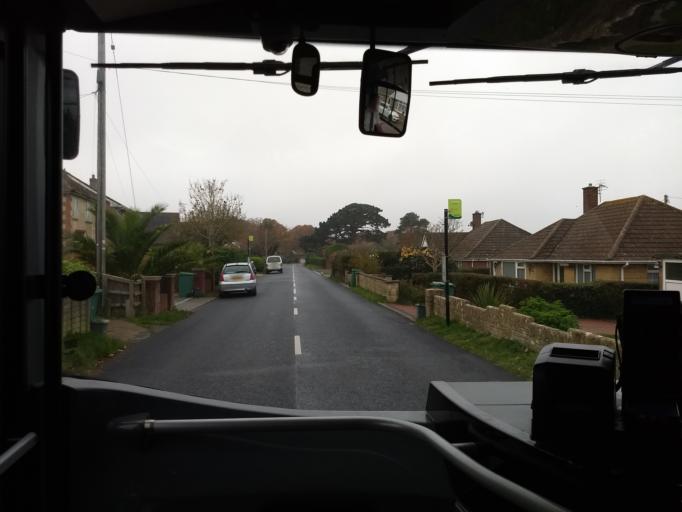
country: GB
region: England
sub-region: Isle of Wight
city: Newchurch
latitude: 50.6544
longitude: -1.2024
